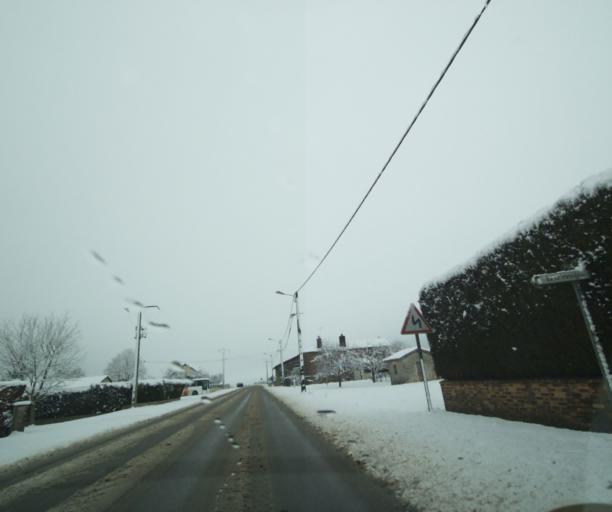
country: FR
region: Champagne-Ardenne
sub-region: Departement de la Haute-Marne
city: Wassy
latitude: 48.5288
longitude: 4.9279
